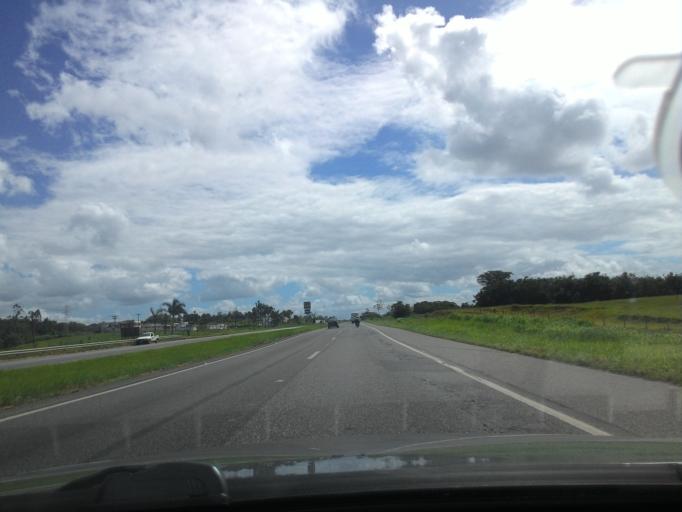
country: BR
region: Sao Paulo
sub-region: Pariquera-Acu
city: Pariquera Acu
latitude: -24.6294
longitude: -47.9030
